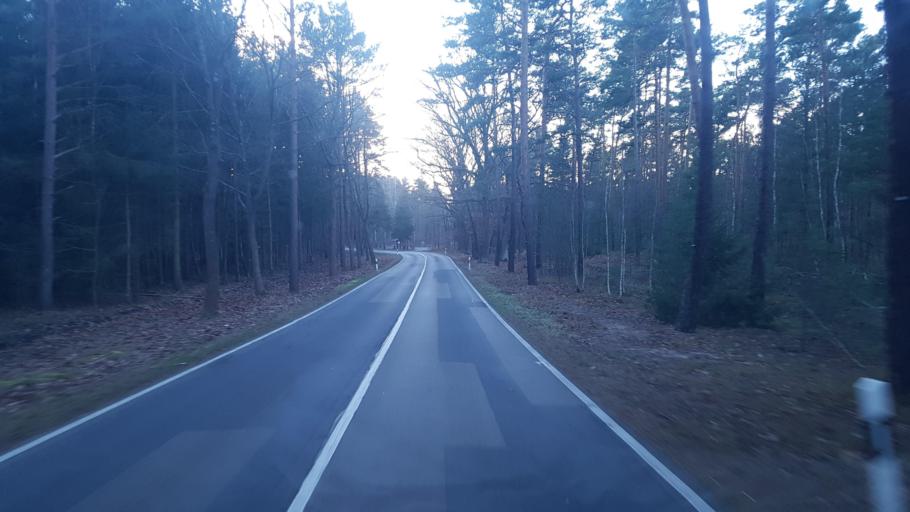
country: DE
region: Brandenburg
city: Drachhausen
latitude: 51.8715
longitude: 14.2750
